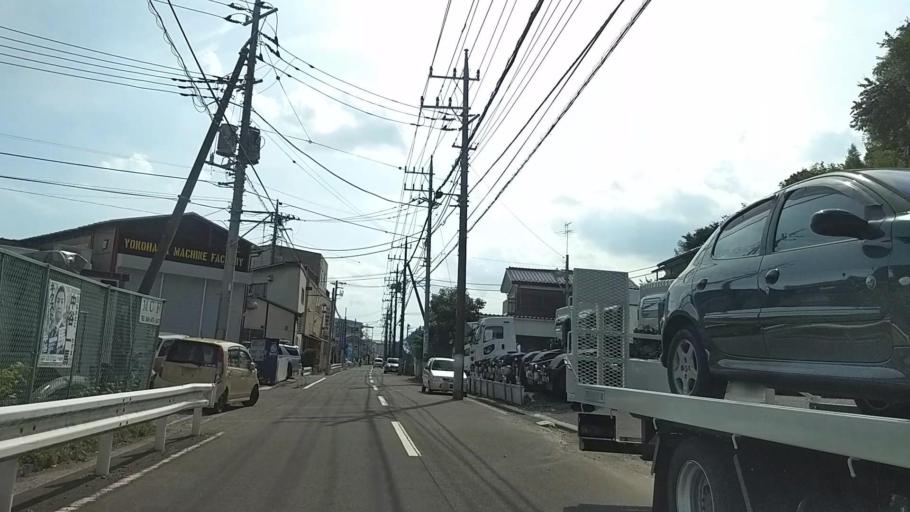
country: JP
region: Kanagawa
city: Yokohama
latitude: 35.5232
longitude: 139.5860
